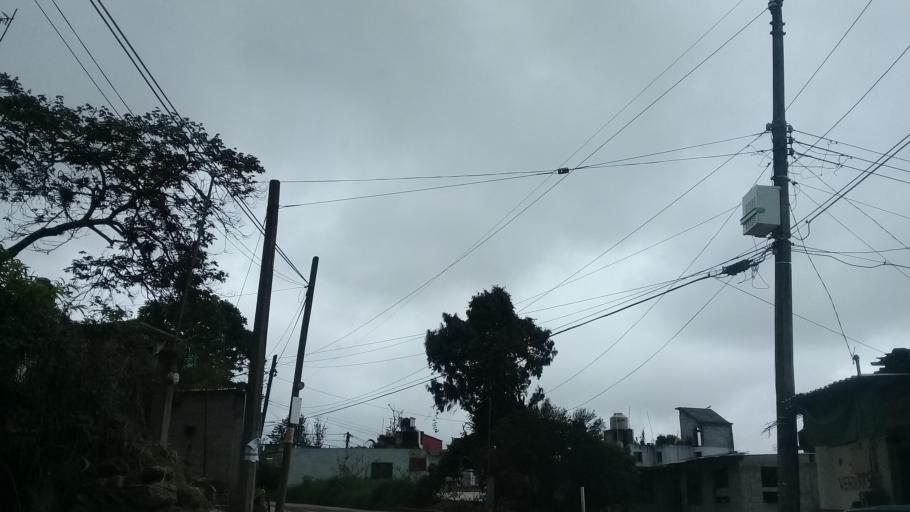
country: MX
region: Veracruz
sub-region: Xalapa
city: Colonia Santa Barbara
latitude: 19.4950
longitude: -96.8702
